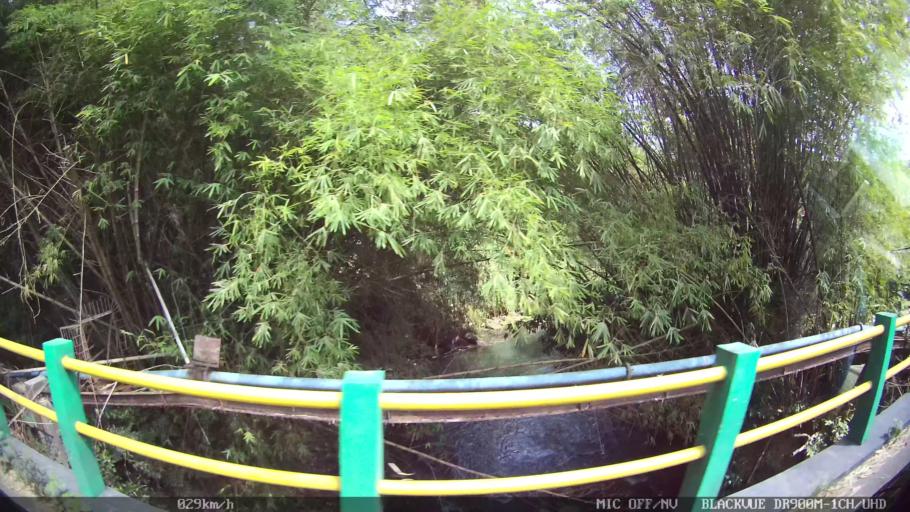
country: ID
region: Daerah Istimewa Yogyakarta
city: Kasihan
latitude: -7.8140
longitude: 110.3350
